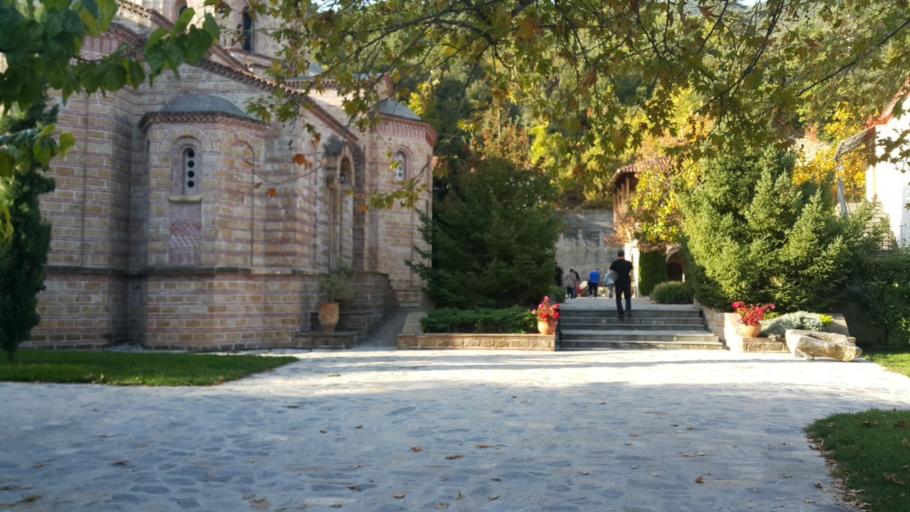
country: GR
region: Central Macedonia
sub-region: Nomos Pierias
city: Litochoro
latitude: 40.1181
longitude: 22.4843
